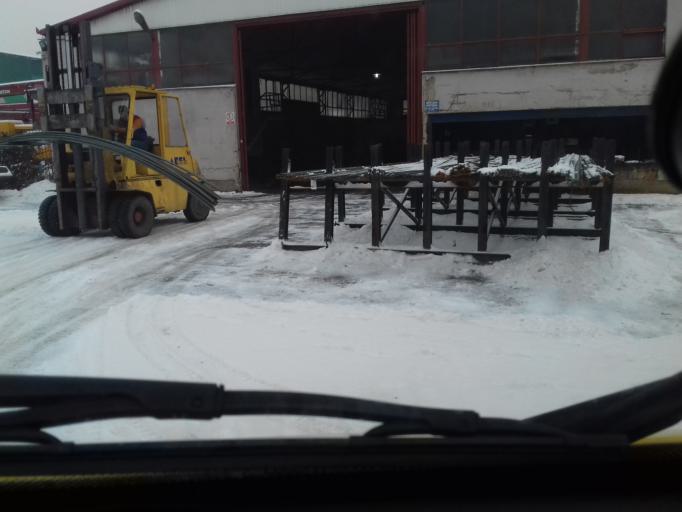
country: BA
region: Federation of Bosnia and Herzegovina
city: Zenica
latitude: 44.1891
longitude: 17.9311
